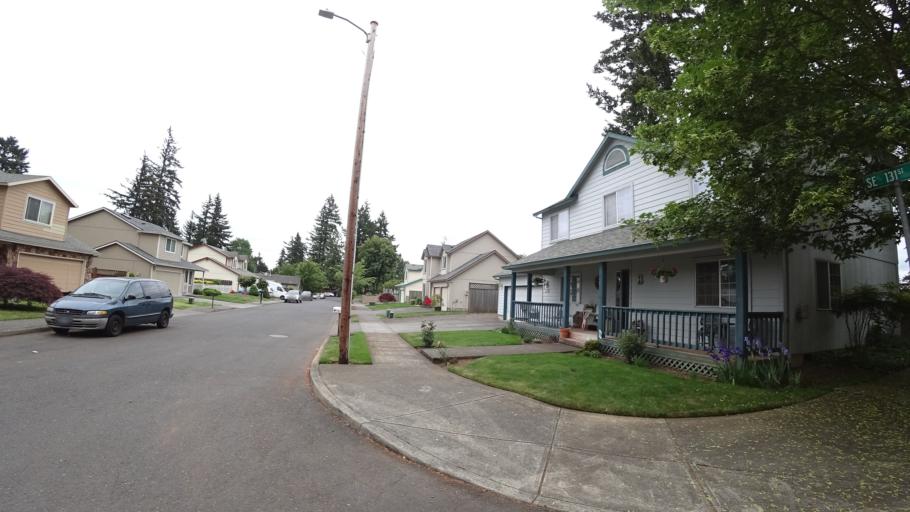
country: US
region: Oregon
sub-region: Multnomah County
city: Lents
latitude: 45.5069
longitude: -122.5284
